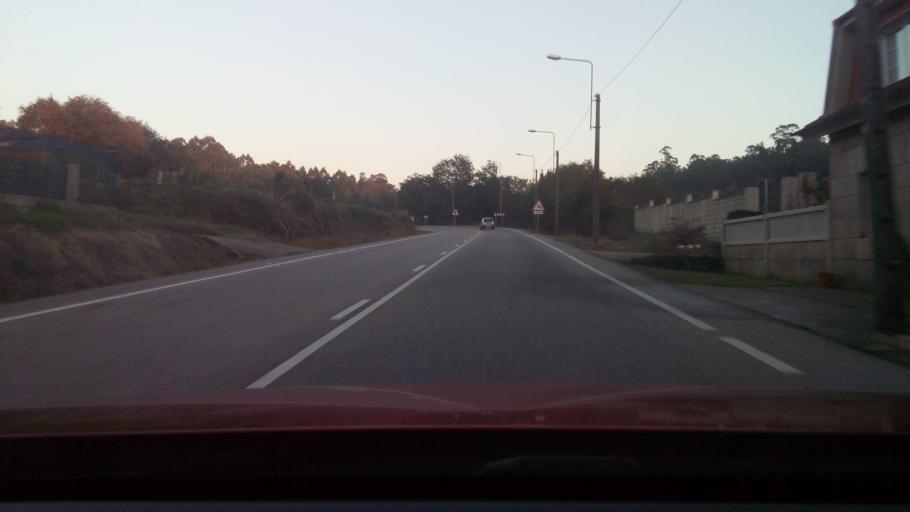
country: ES
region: Galicia
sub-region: Provincia de Pontevedra
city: Gondomar
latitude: 42.1583
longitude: -8.7097
